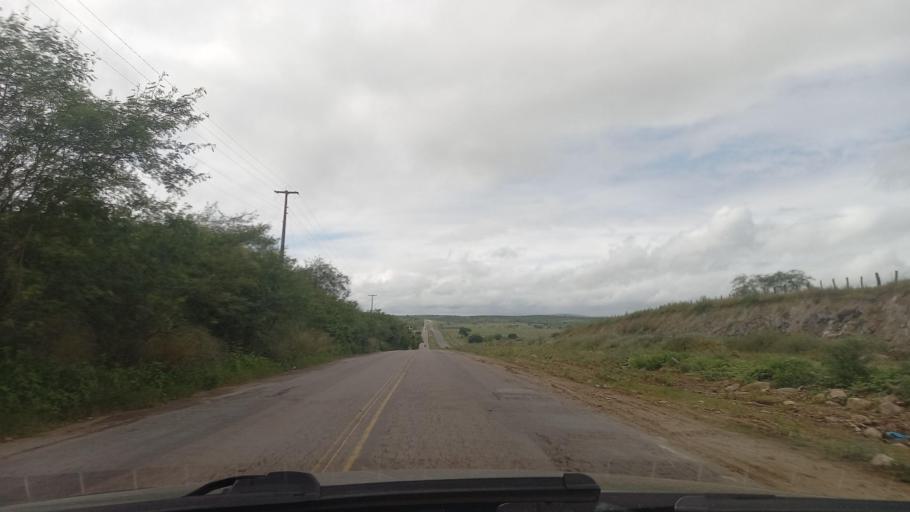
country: BR
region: Alagoas
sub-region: Batalha
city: Batalha
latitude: -9.6481
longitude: -37.1864
